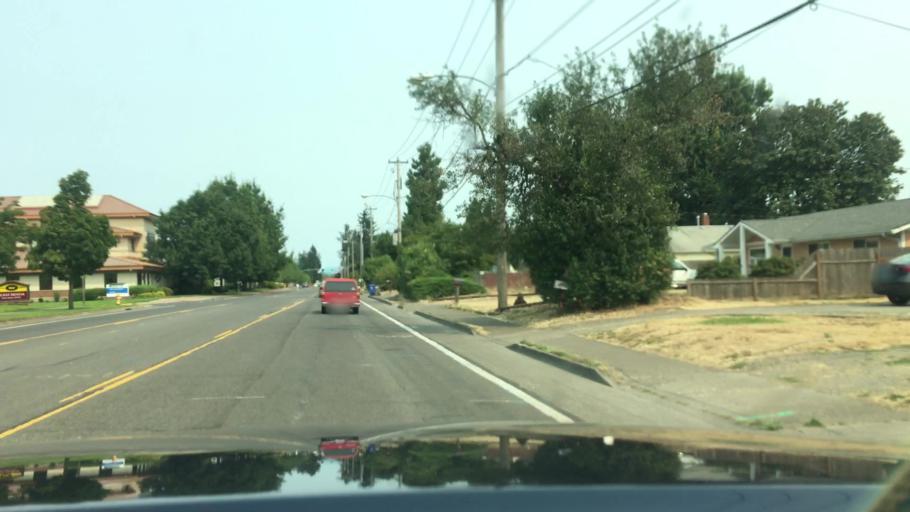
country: US
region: Oregon
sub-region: Lane County
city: Eugene
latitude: 44.0845
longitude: -123.1652
